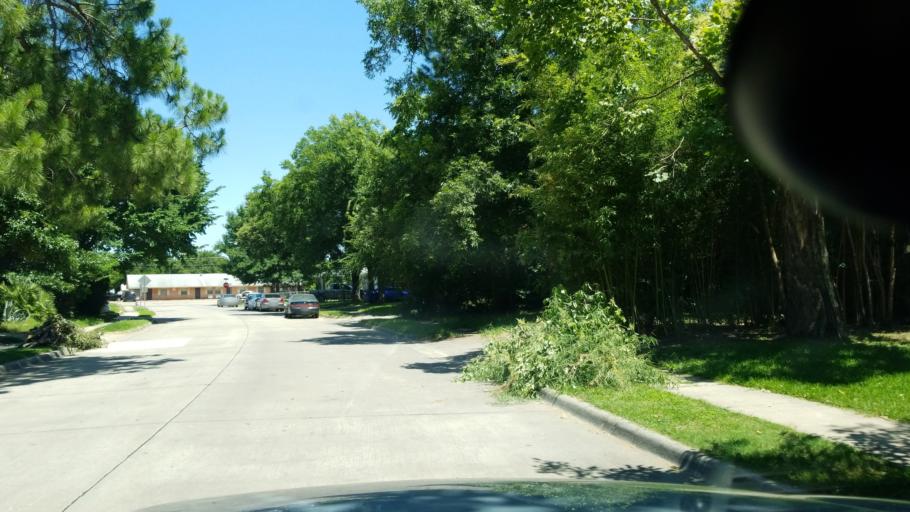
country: US
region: Texas
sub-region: Dallas County
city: Irving
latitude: 32.8314
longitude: -96.9316
